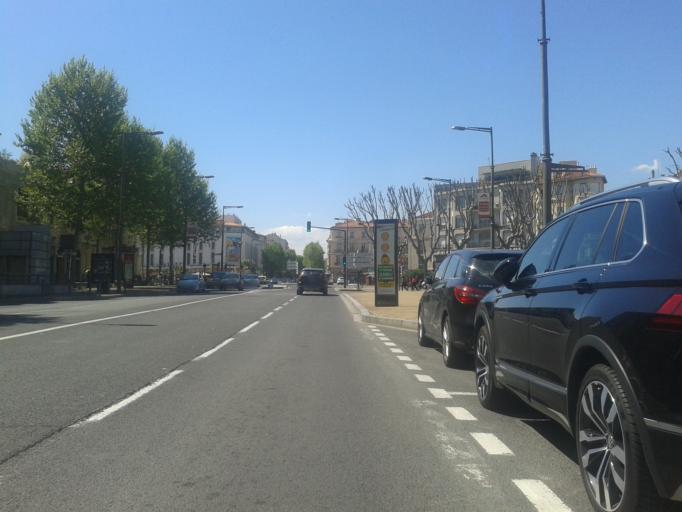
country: FR
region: Languedoc-Roussillon
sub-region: Departement des Pyrenees-Orientales
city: Perpignan
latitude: 42.7018
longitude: 2.8951
